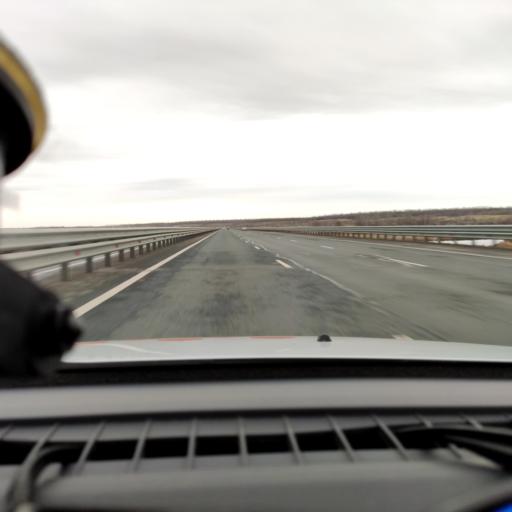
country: RU
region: Samara
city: Smyshlyayevka
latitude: 53.1570
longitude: 50.3381
